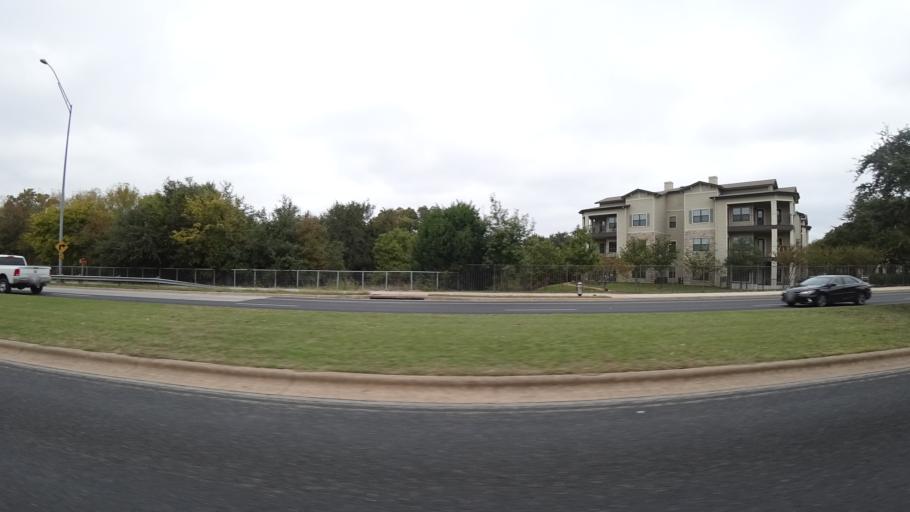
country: US
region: Texas
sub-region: Williamson County
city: Anderson Mill
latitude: 30.4752
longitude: -97.8122
